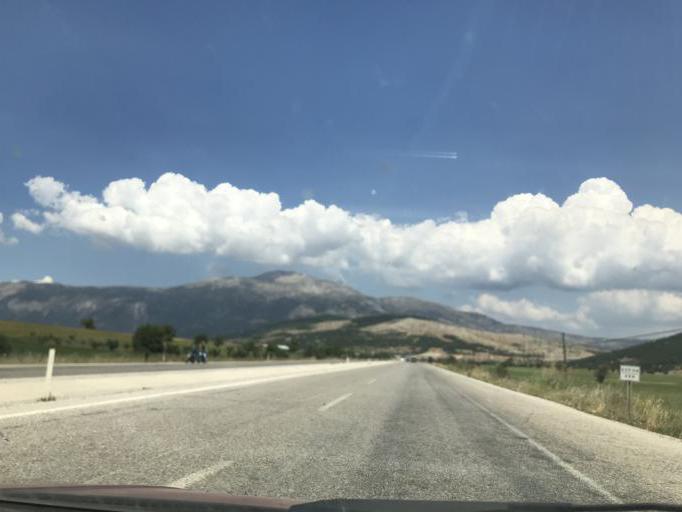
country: TR
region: Denizli
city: Serinhisar
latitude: 37.6217
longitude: 29.1964
